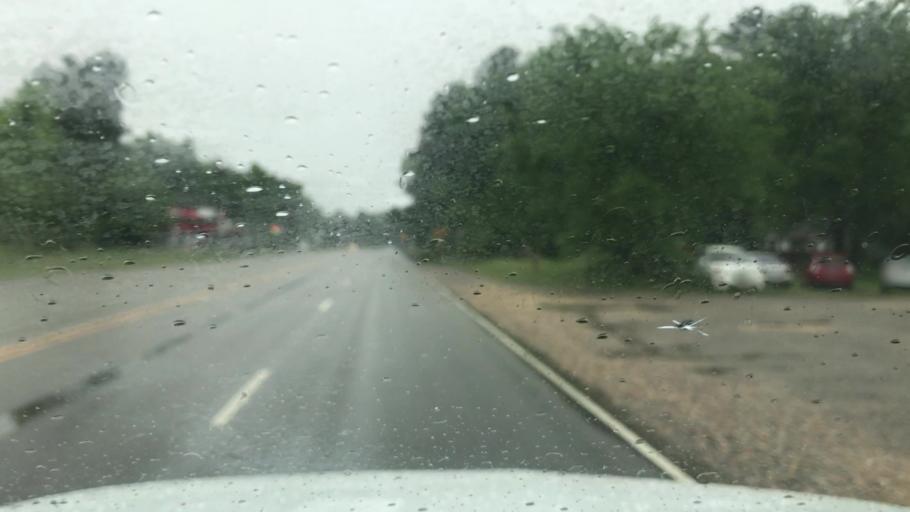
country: US
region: Virginia
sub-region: Hanover County
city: Ashland
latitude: 37.8162
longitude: -77.4740
